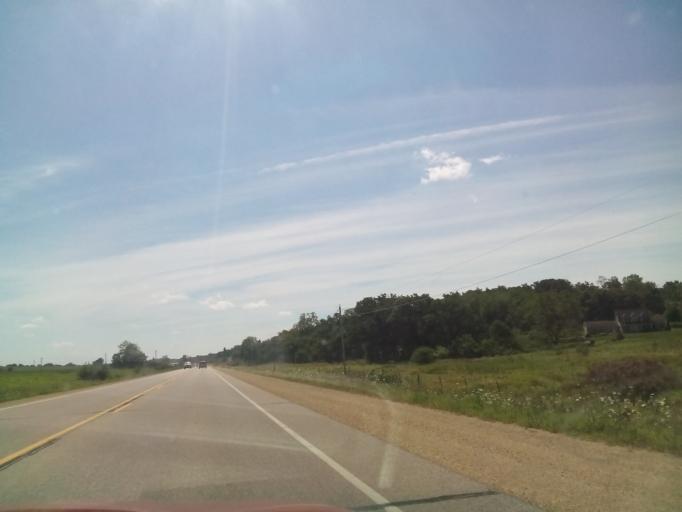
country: US
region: Wisconsin
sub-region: Green County
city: Monticello
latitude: 42.7632
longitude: -89.6186
